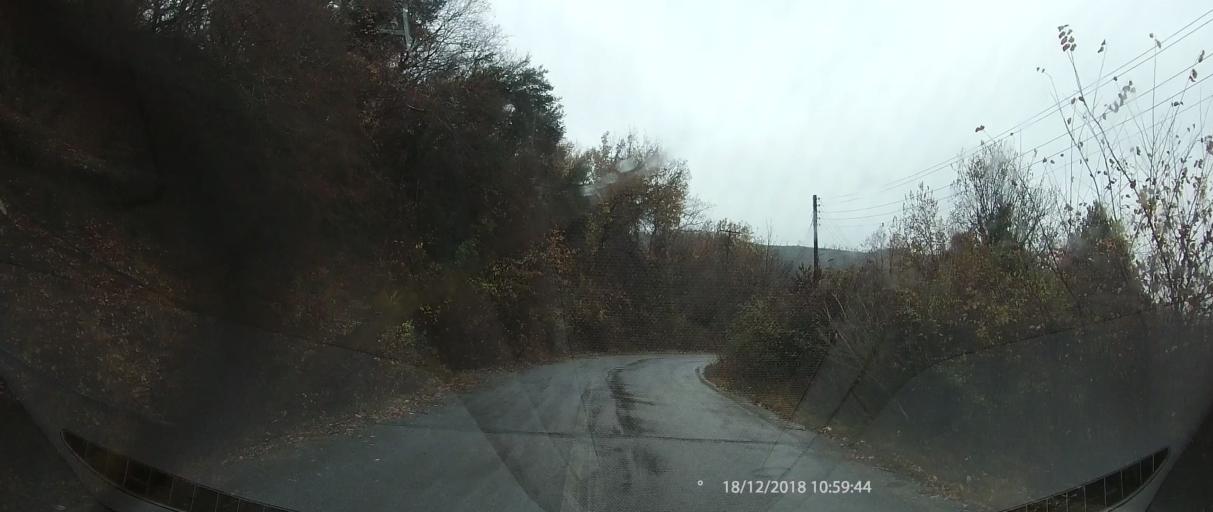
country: GR
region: Central Macedonia
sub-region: Nomos Pierias
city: Kato Milia
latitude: 40.1973
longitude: 22.3192
